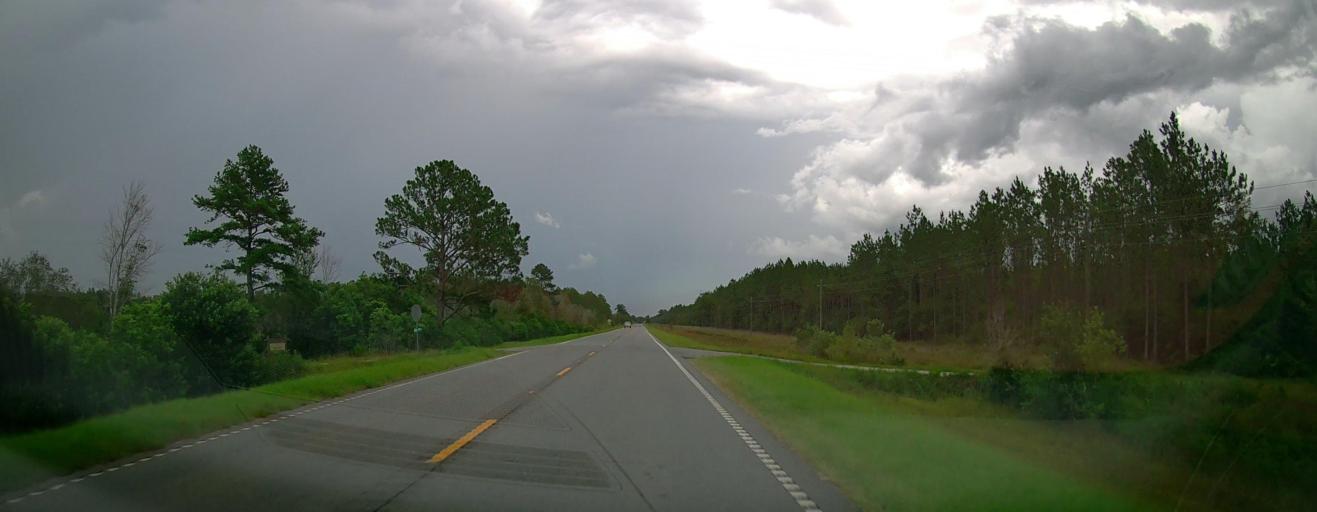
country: US
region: Georgia
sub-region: Brantley County
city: Nahunta
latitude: 31.3540
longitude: -82.0467
